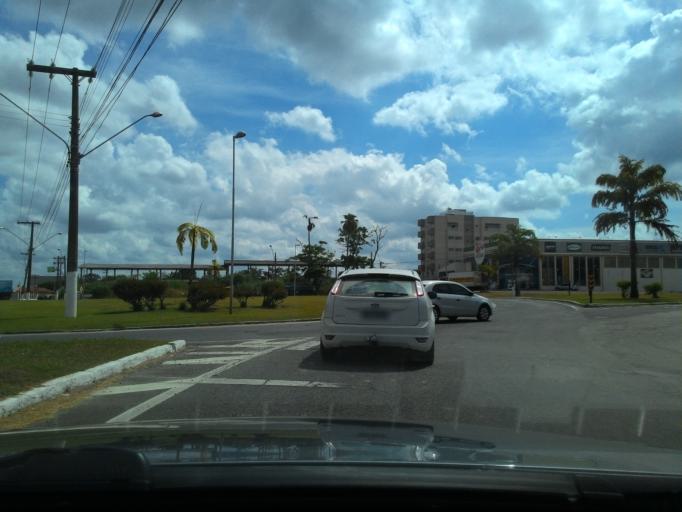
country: BR
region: Sao Paulo
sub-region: Registro
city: Registro
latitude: -24.5017
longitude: -47.8538
